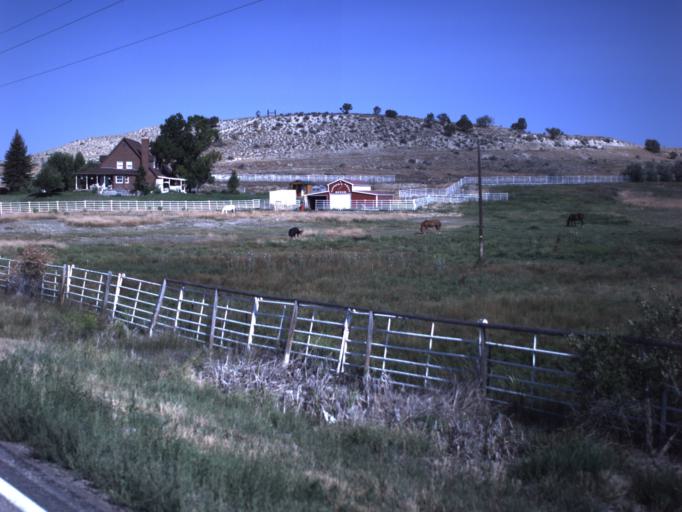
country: US
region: Utah
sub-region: Sanpete County
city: Mount Pleasant
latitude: 39.5468
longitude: -111.5201
